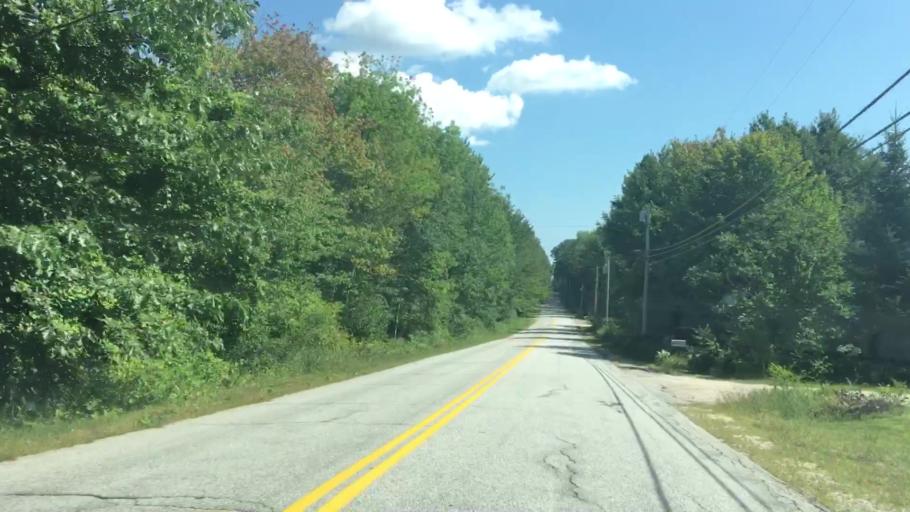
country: US
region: Maine
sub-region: Cumberland County
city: New Gloucester
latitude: 43.9402
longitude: -70.2958
